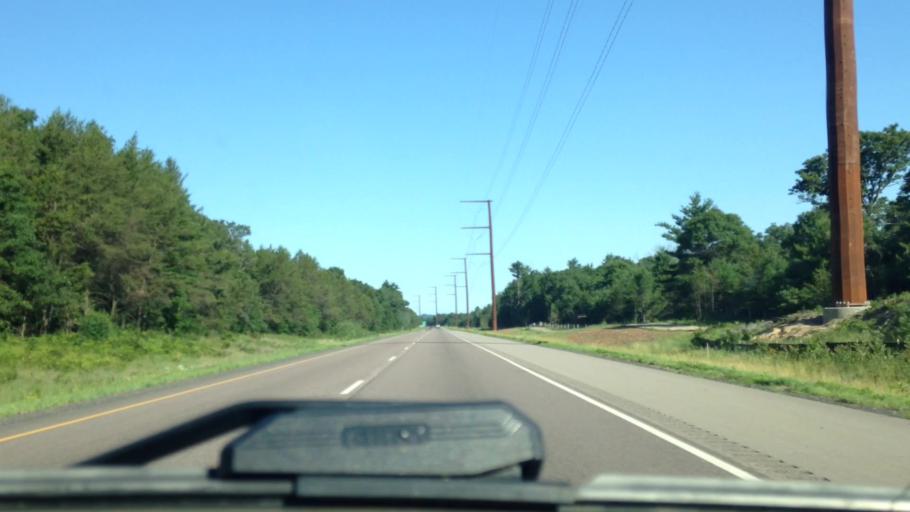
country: US
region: Wisconsin
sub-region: Monroe County
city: Tomah
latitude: 44.1767
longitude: -90.6049
